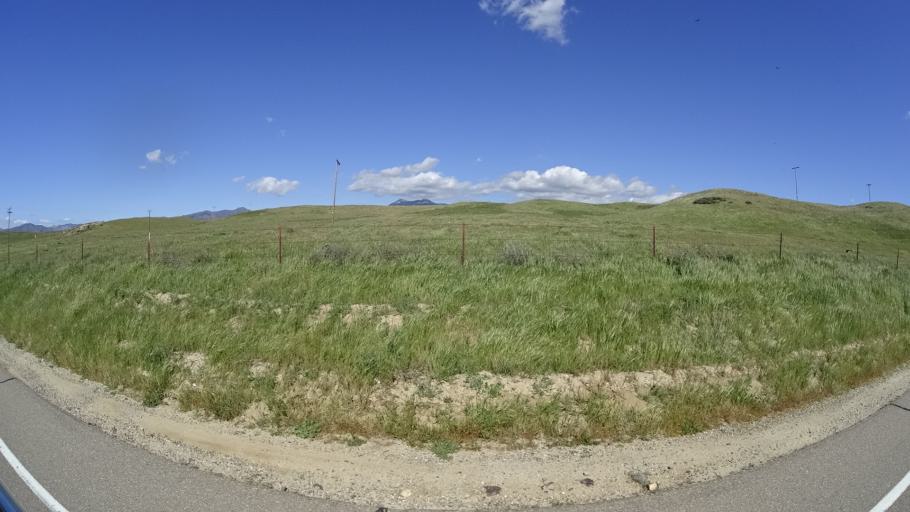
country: US
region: California
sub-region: San Diego County
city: Julian
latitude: 33.2477
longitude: -116.6728
